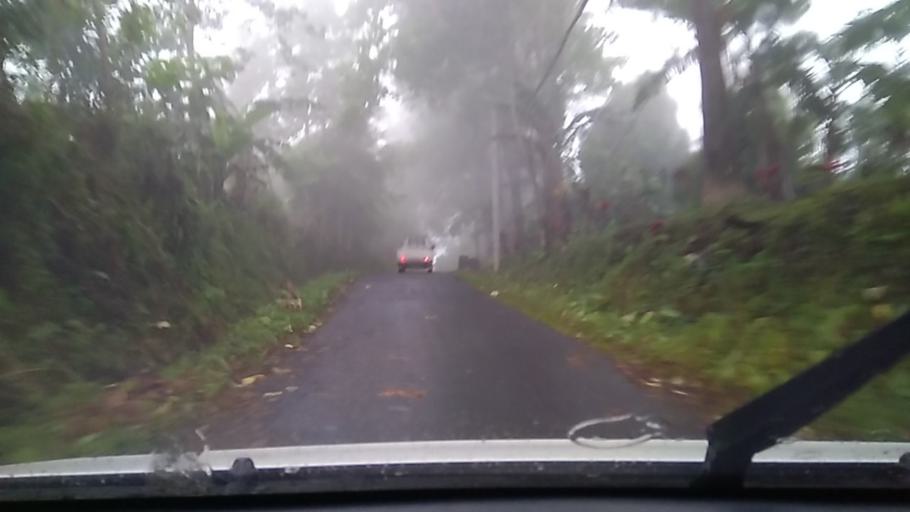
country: ID
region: Bali
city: Banjar Ambengan
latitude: -8.2051
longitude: 115.1727
